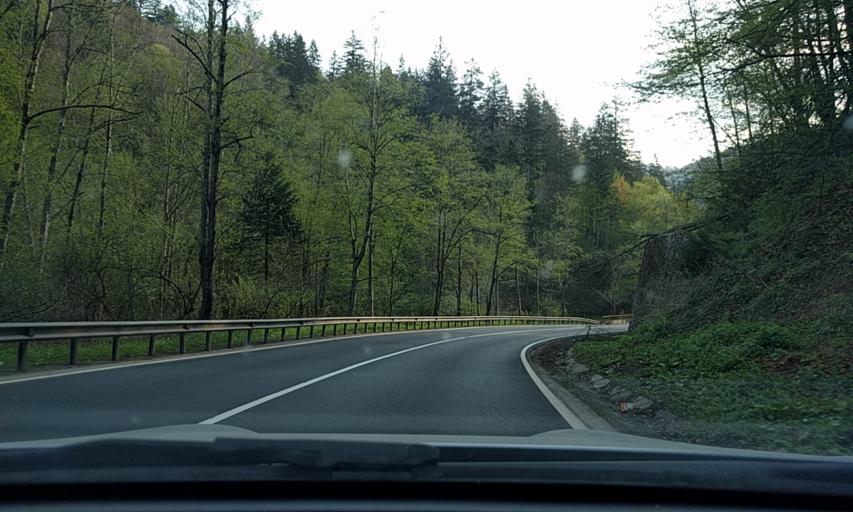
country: RO
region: Covasna
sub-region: Comuna Bretcu
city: Bretcu
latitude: 46.0869
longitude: 26.4002
